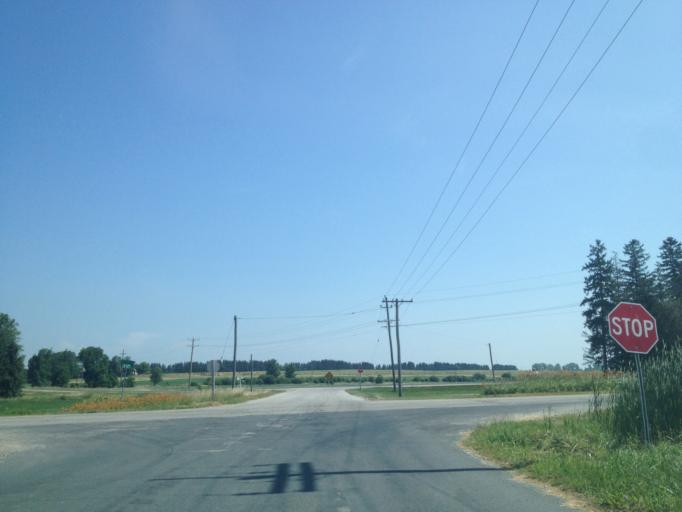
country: CA
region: Ontario
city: Stratford
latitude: 43.2708
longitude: -81.1945
